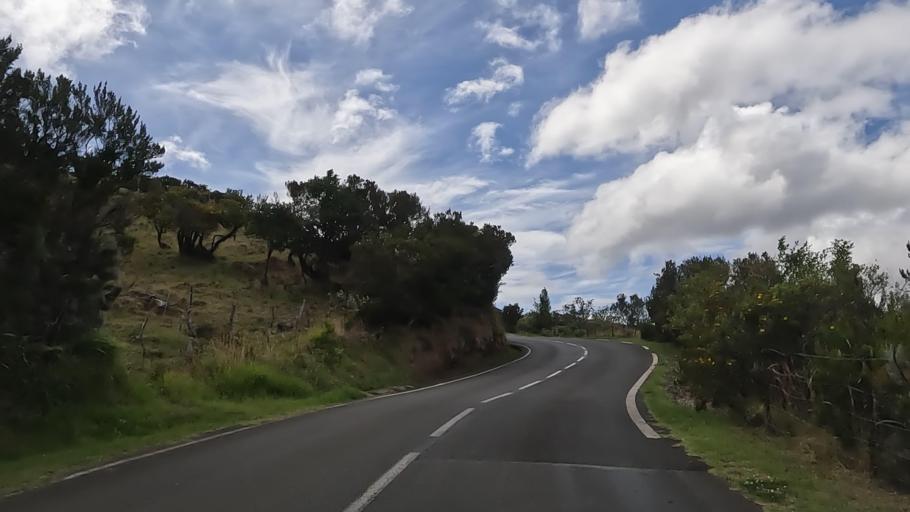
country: RE
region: Reunion
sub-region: Reunion
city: Le Tampon
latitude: -21.2441
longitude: 55.5891
